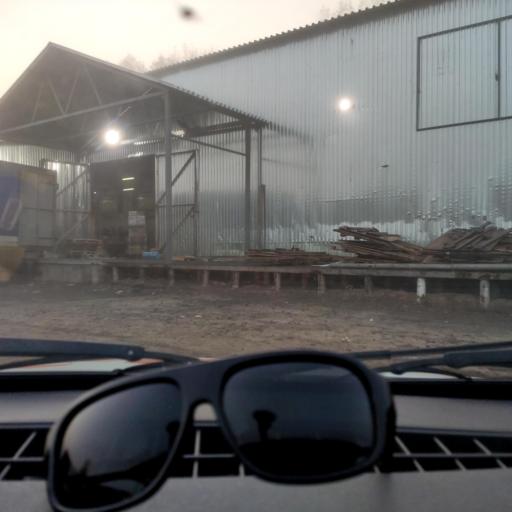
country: RU
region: Bashkortostan
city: Ufa
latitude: 54.7881
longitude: 56.0896
